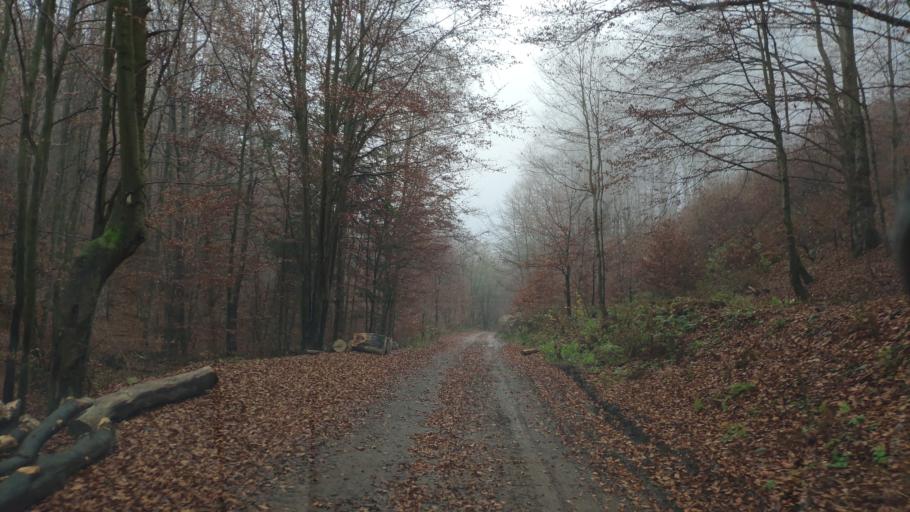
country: SK
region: Presovsky
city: Sabinov
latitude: 49.1593
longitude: 21.1990
